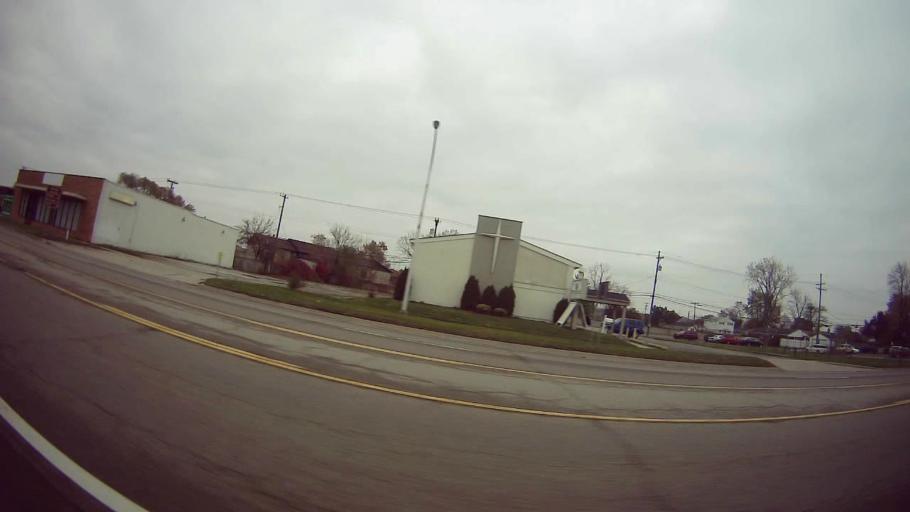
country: US
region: Michigan
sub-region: Oakland County
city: Madison Heights
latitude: 42.5182
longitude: -83.1065
